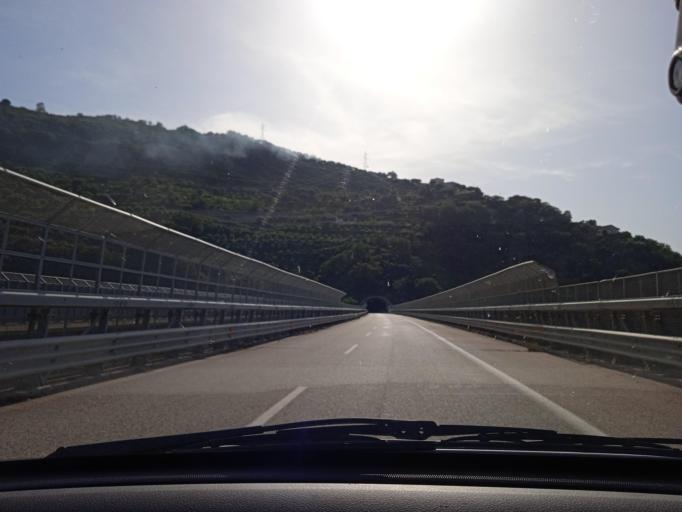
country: IT
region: Sicily
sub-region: Messina
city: Brolo
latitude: 38.1455
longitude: 14.8033
